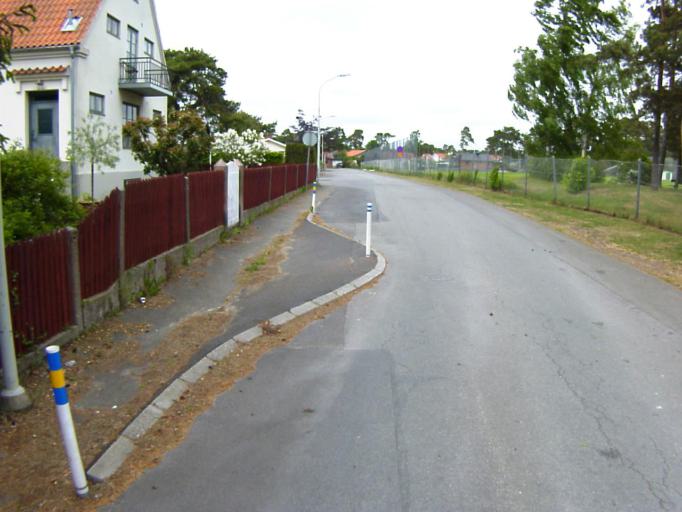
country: SE
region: Skane
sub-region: Kristianstads Kommun
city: Ahus
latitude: 55.9303
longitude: 14.2987
